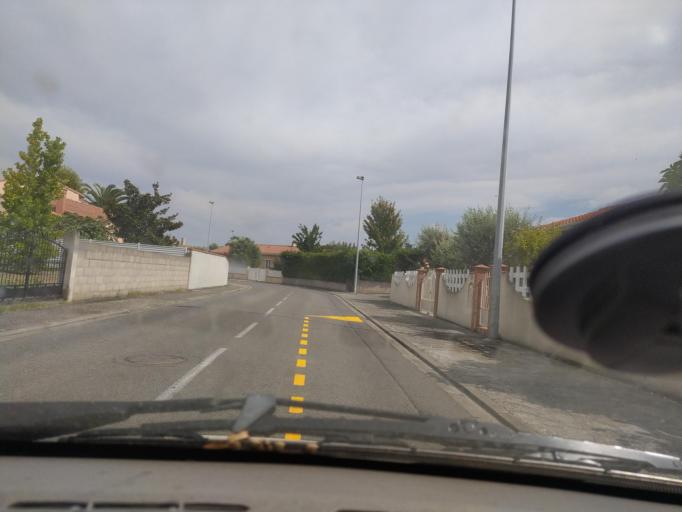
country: FR
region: Midi-Pyrenees
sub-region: Departement de la Haute-Garonne
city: Tournefeuille
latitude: 43.5919
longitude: 1.3192
